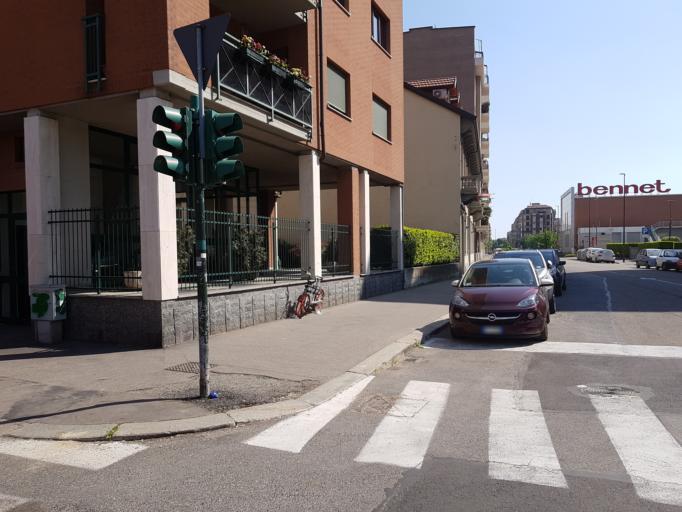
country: IT
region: Piedmont
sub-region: Provincia di Torino
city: Lesna
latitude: 45.0611
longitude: 7.6417
